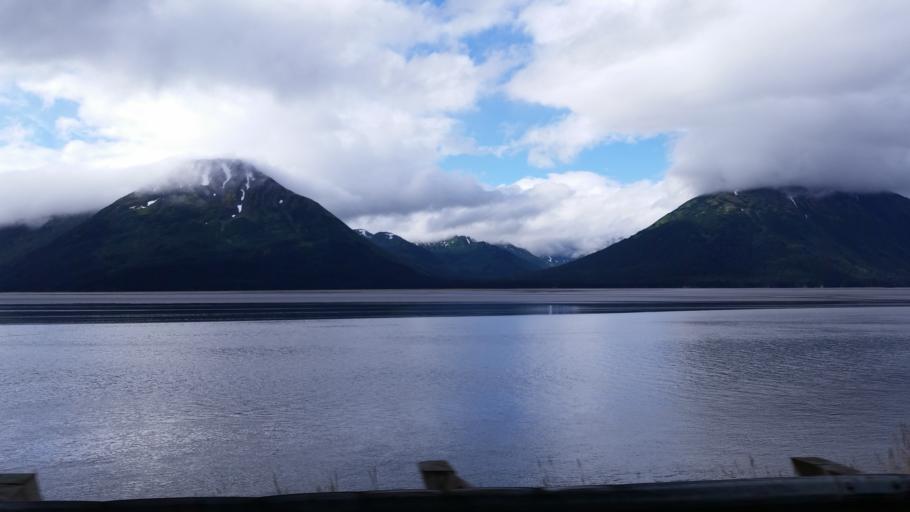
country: US
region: Alaska
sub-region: Anchorage Municipality
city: Girdwood
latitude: 60.9162
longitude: -149.1133
